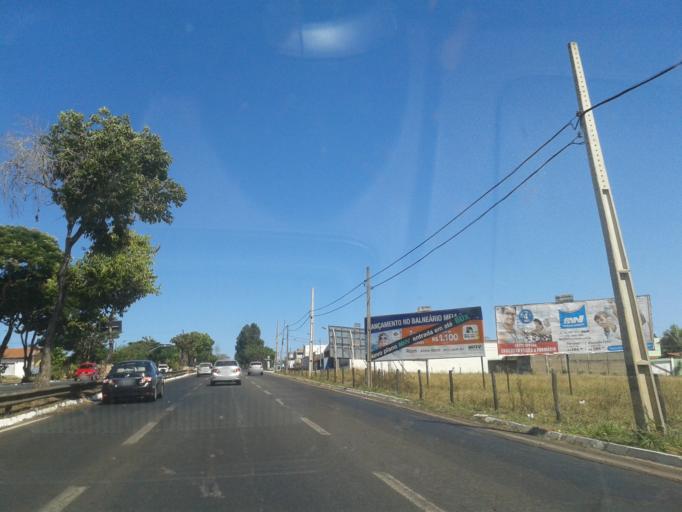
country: BR
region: Goias
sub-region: Goiania
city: Goiania
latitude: -16.6359
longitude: -49.2835
